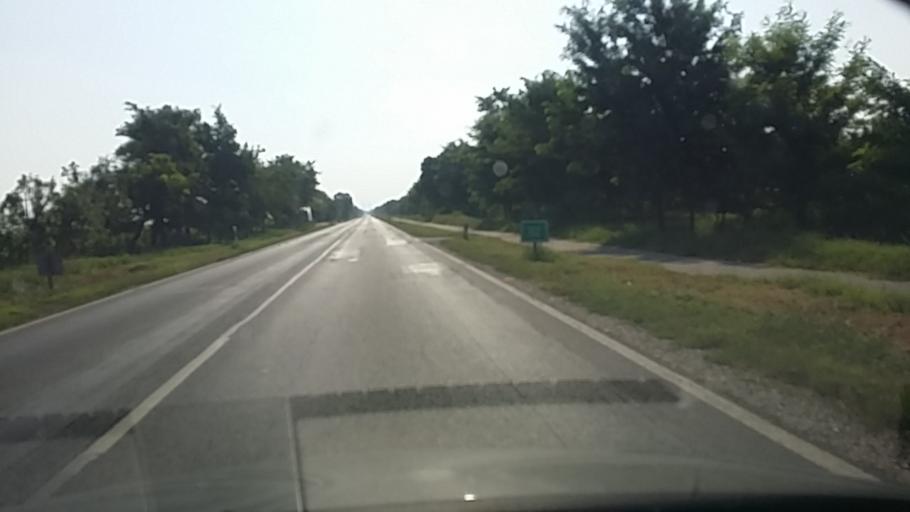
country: HU
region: Bekes
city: Mezobereny
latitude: 46.7105
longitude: 20.9730
